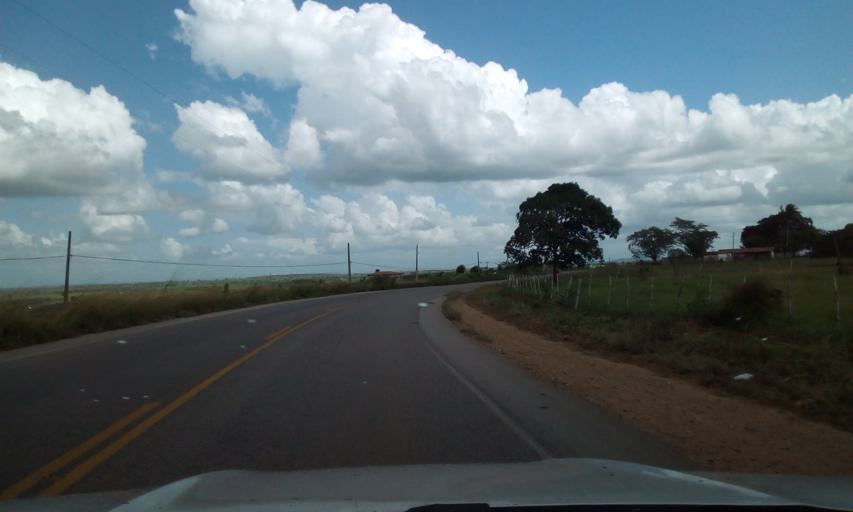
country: BR
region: Paraiba
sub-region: Guarabira
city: Guarabira
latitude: -6.8453
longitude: -35.3592
